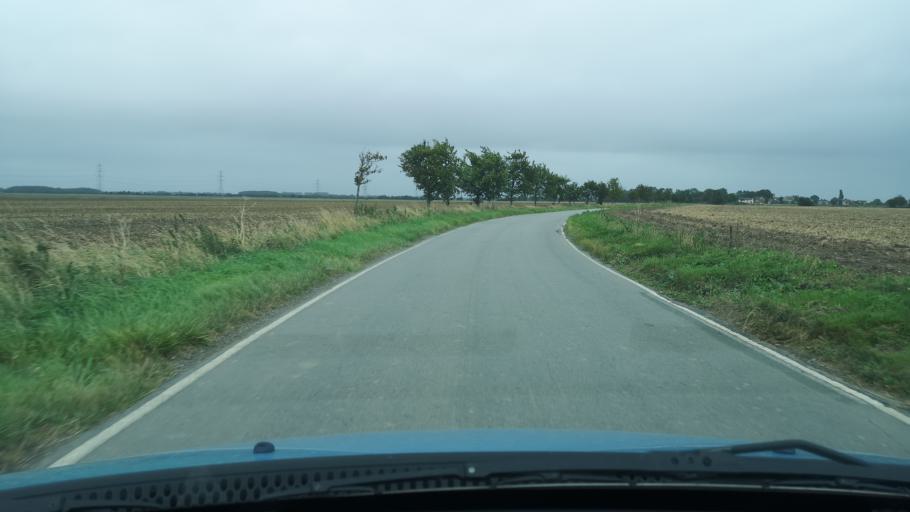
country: GB
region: England
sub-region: North Lincolnshire
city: Burton upon Stather
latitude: 53.6682
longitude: -0.7211
